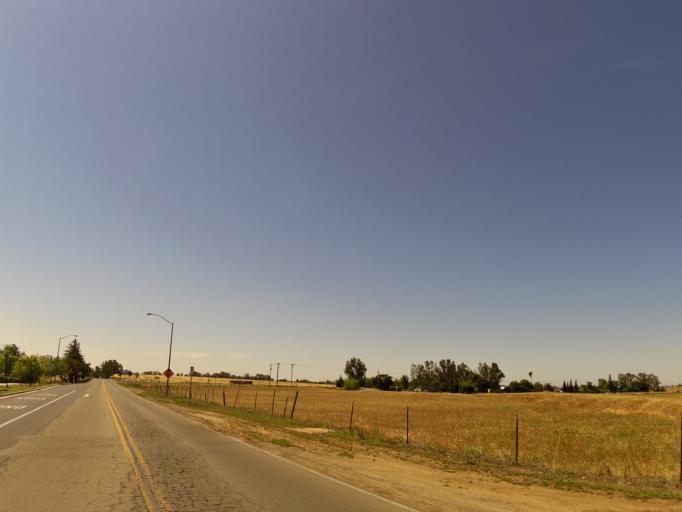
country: US
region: California
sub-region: Merced County
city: Merced
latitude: 37.3634
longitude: -120.4323
